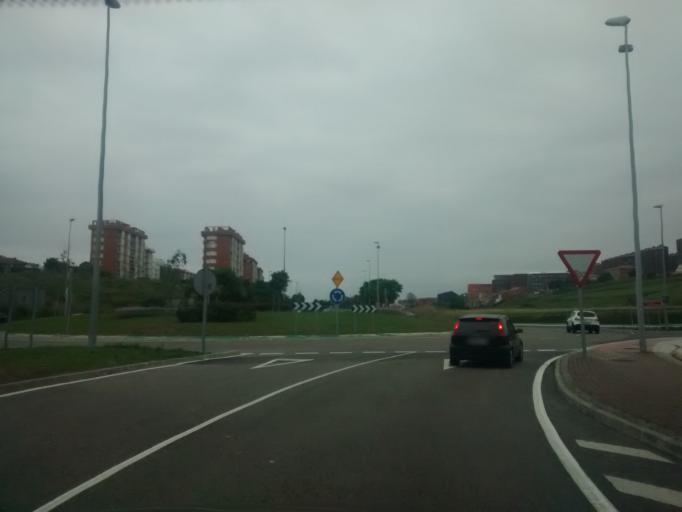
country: ES
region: Cantabria
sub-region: Provincia de Cantabria
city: Santander
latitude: 43.4709
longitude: -3.8174
